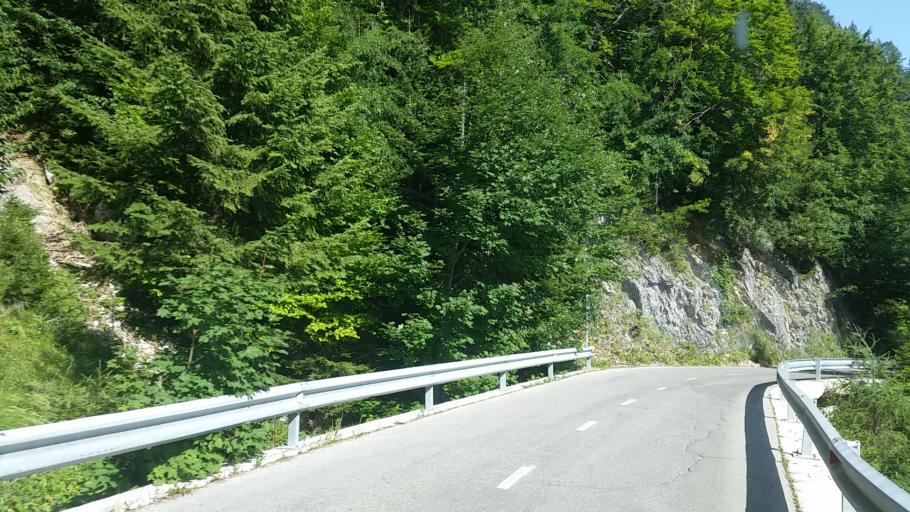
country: SI
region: Kranjska Gora
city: Kranjska Gora
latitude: 46.4144
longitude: 13.7440
